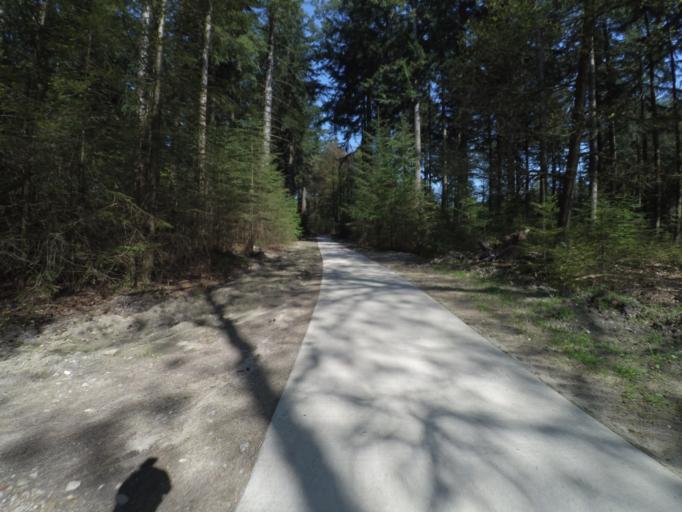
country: NL
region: Gelderland
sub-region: Gemeente Apeldoorn
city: Apeldoorn
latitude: 52.2044
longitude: 5.8971
